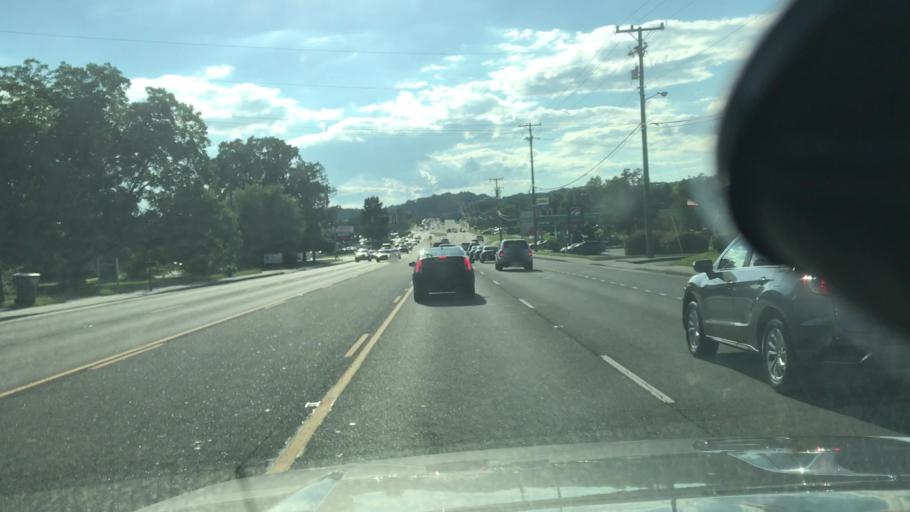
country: US
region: Tennessee
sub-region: Davidson County
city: Belle Meade
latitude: 36.0765
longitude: -86.9436
